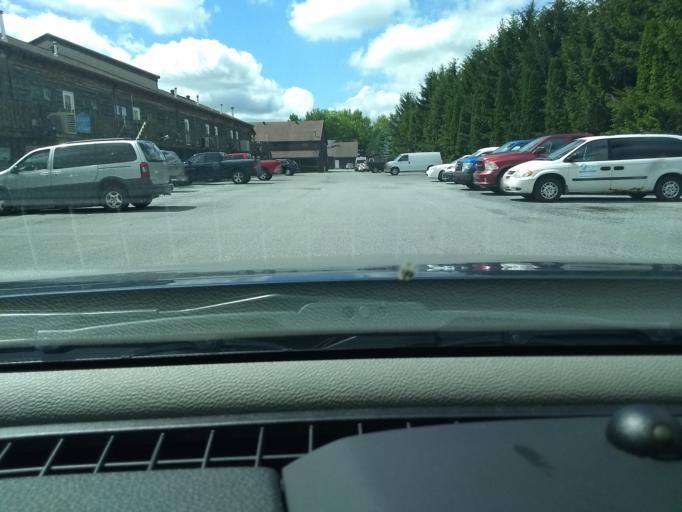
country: US
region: Pennsylvania
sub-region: Cambria County
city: Ebensburg
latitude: 40.4621
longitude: -78.7515
